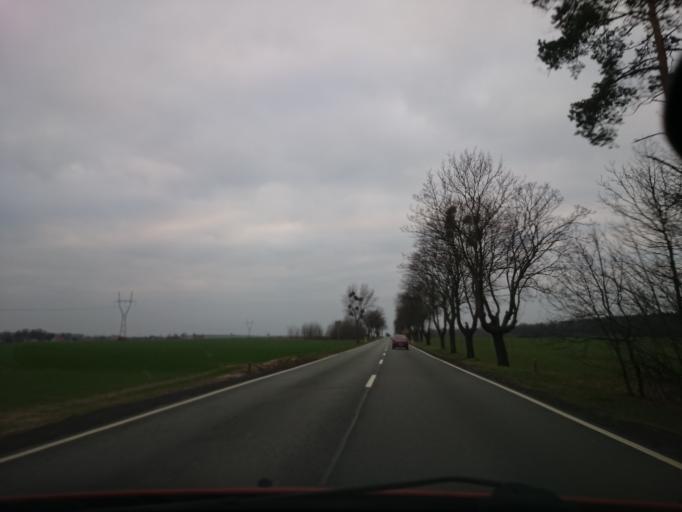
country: PL
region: Opole Voivodeship
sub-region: Powiat nyski
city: Lambinowice
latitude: 50.6090
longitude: 17.5563
